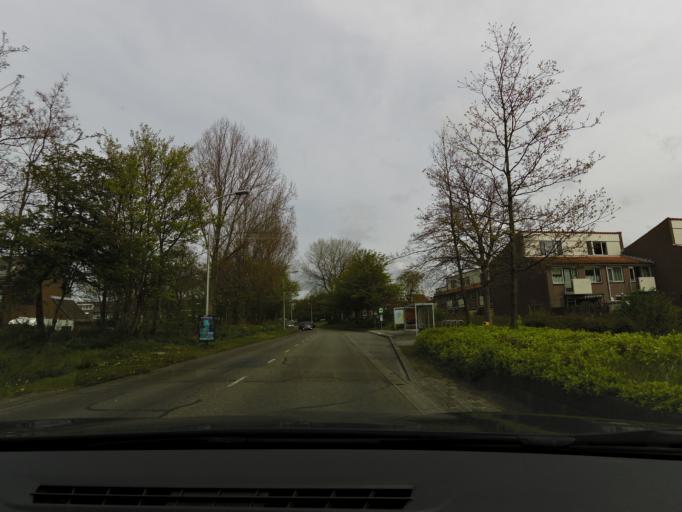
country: NL
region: South Holland
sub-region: Gemeente Katwijk
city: Katwijk aan den Rijn
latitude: 52.2076
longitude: 4.4221
